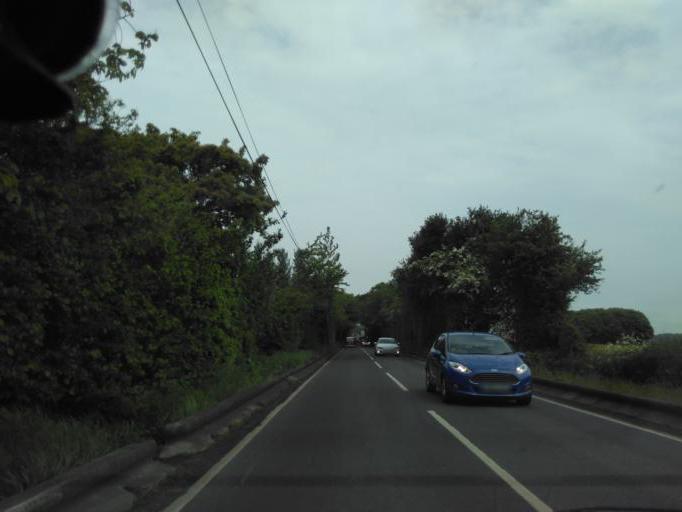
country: GB
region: England
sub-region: Kent
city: Lyminge
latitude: 51.1806
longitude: 1.0538
